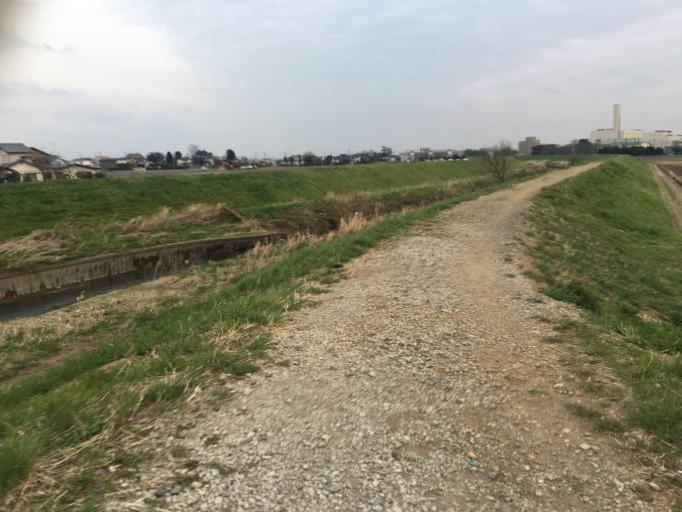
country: JP
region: Saitama
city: Kamifukuoka
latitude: 35.8774
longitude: 139.5420
